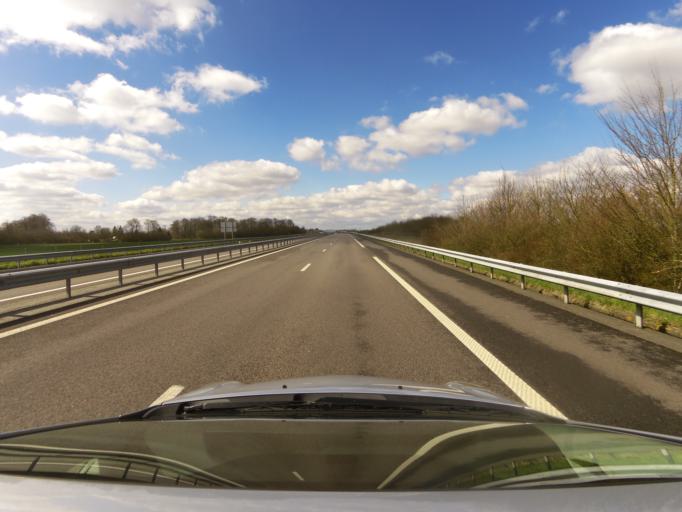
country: FR
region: Haute-Normandie
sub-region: Departement de la Seine-Maritime
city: Totes
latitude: 49.6389
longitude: 1.0684
